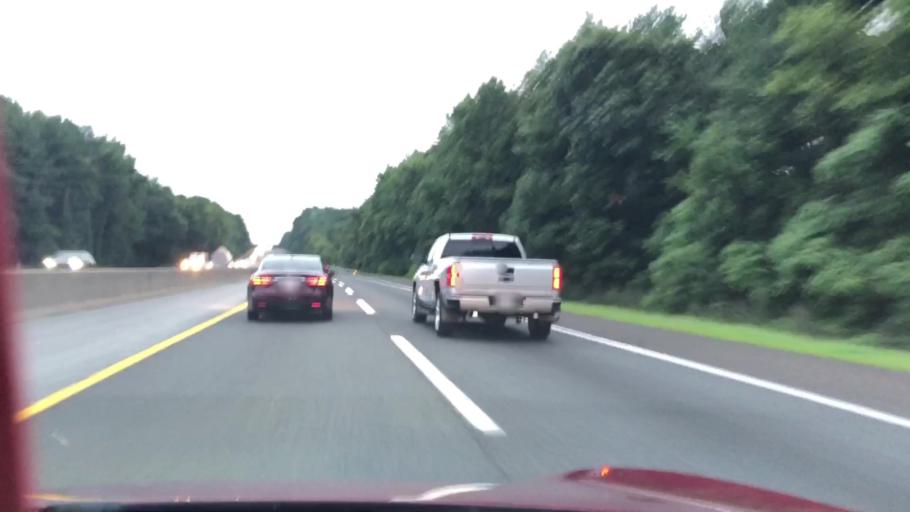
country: US
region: New Jersey
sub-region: Gloucester County
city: Oak Valley
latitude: 39.8039
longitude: -75.1899
